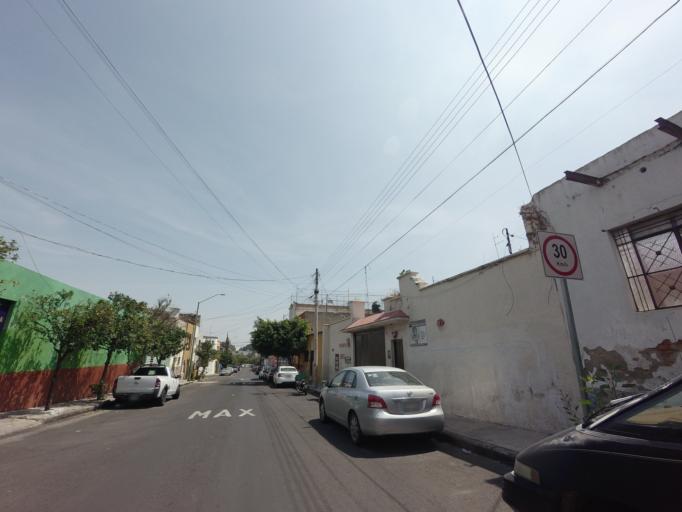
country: MX
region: Jalisco
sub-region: Zapopan
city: Zapopan
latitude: 20.6902
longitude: -103.3458
